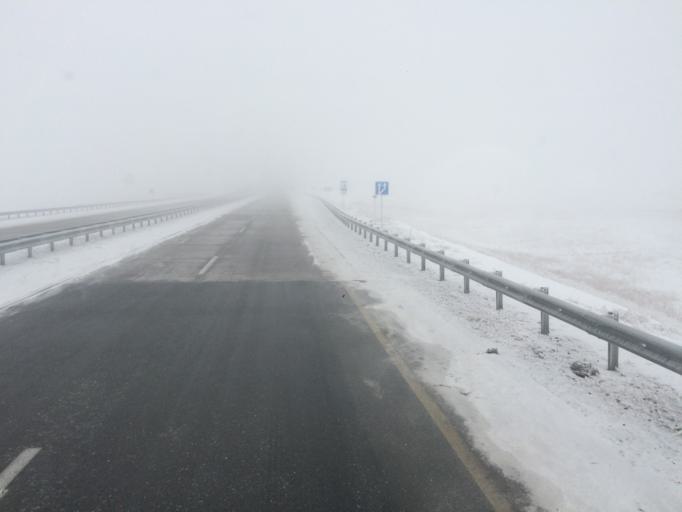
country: KZ
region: Zhambyl
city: Georgiyevka
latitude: 43.4322
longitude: 74.9393
